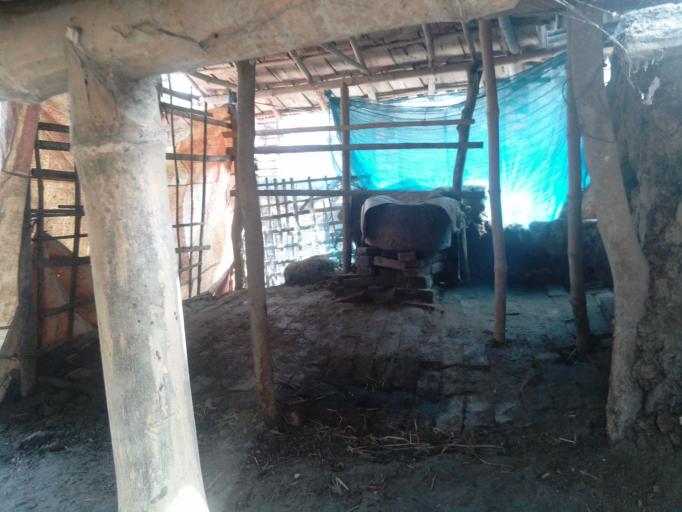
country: BD
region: Khulna
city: Kesabpur
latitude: 22.7820
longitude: 89.2746
